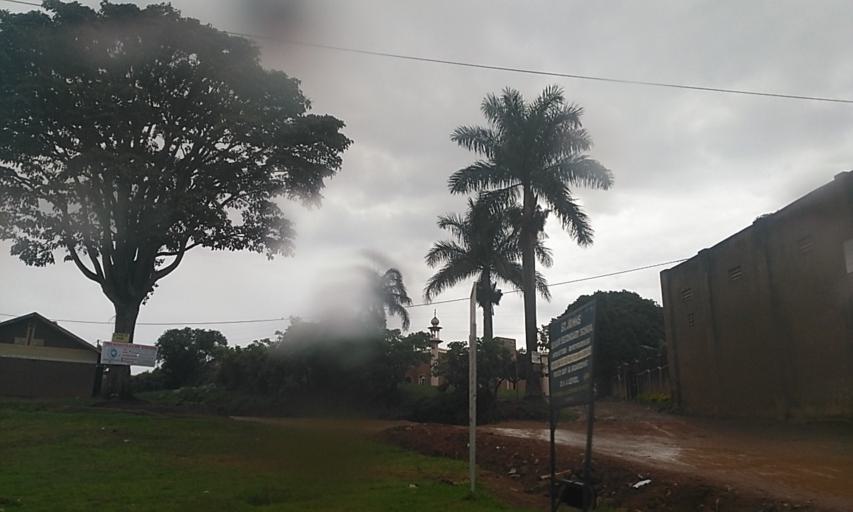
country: UG
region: Central Region
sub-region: Wakiso District
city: Kireka
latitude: 0.3517
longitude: 32.6572
